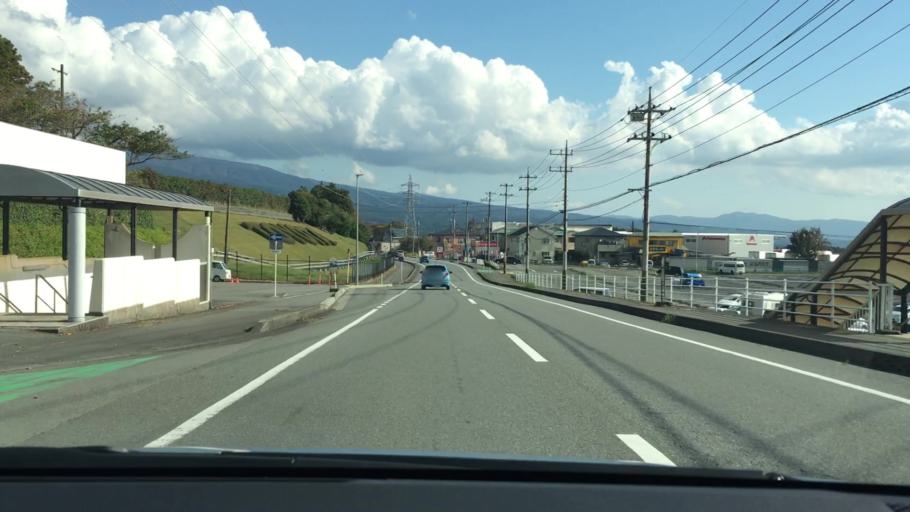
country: JP
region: Shizuoka
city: Gotemba
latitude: 35.2231
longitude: 138.8971
